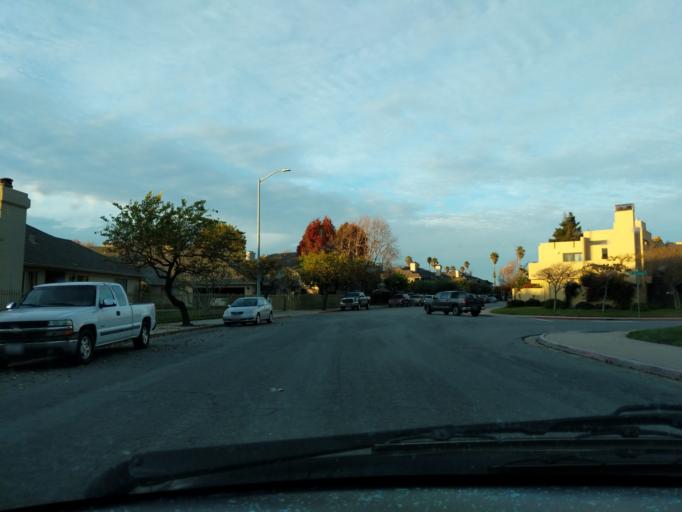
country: US
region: California
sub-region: Monterey County
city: Salinas
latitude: 36.6594
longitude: -121.6614
